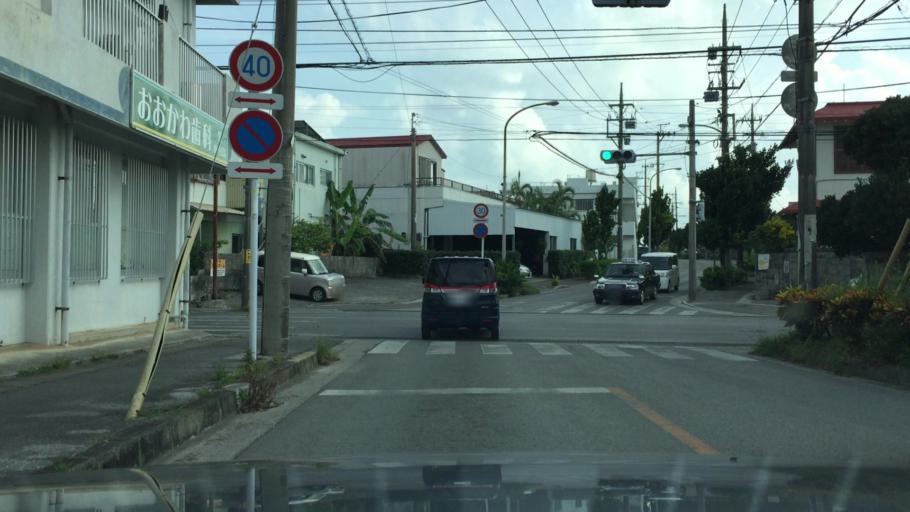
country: JP
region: Okinawa
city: Ishigaki
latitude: 24.3464
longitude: 124.1618
